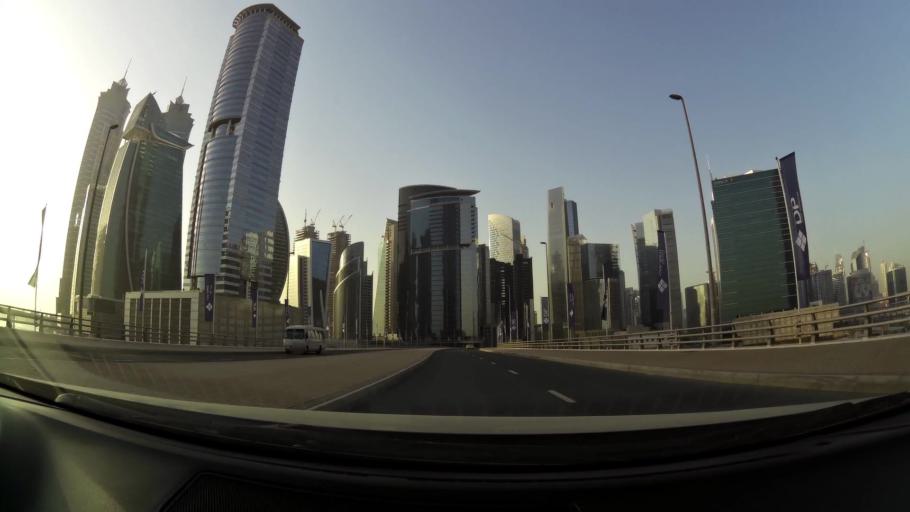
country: AE
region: Dubai
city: Dubai
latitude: 25.1820
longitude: 55.2618
